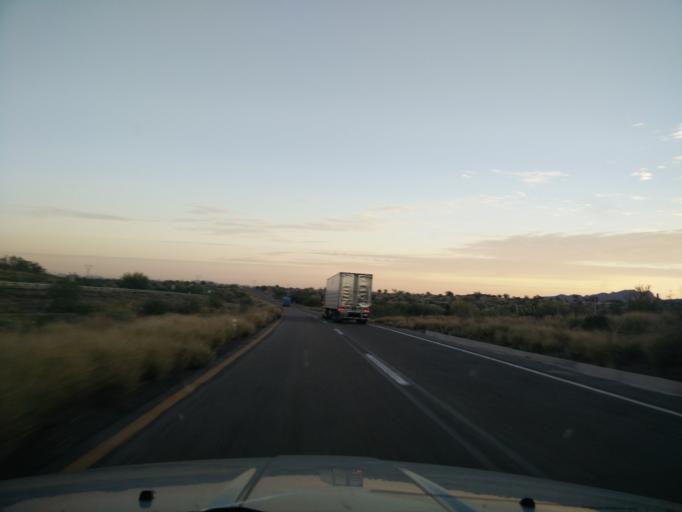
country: MX
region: Sonora
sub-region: Hermosillo
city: Miguel Aleman (La Doce)
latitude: 28.5134
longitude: -111.0456
